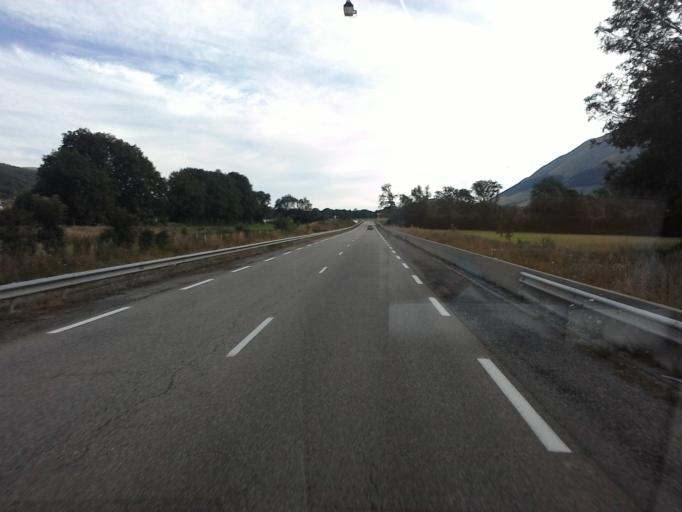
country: FR
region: Rhone-Alpes
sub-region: Departement de l'Isere
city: Pierre-Chatel
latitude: 44.9514
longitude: 5.7804
